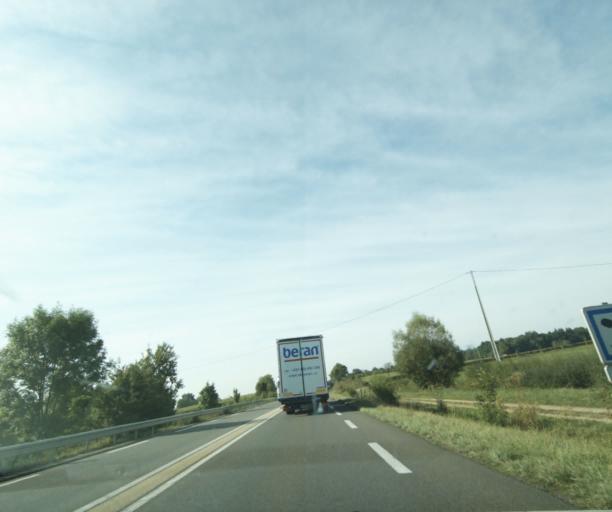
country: FR
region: Bourgogne
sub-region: Departement de Saone-et-Loire
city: Genelard
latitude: 46.5803
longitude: 4.2152
